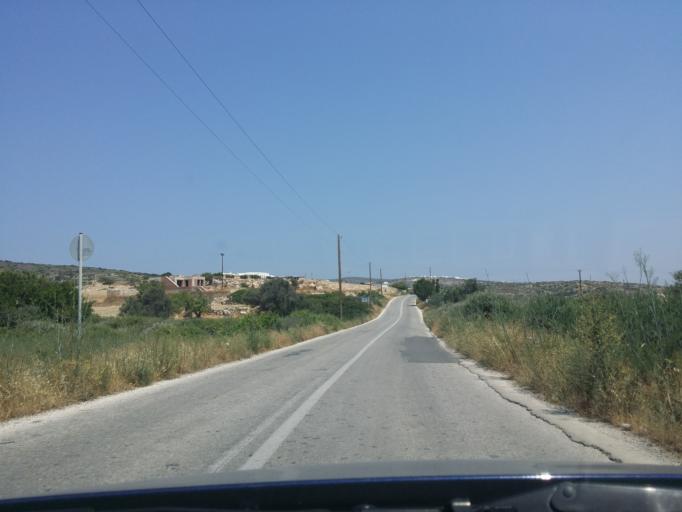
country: GR
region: South Aegean
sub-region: Nomos Kykladon
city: Naousa
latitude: 37.0537
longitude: 25.2391
